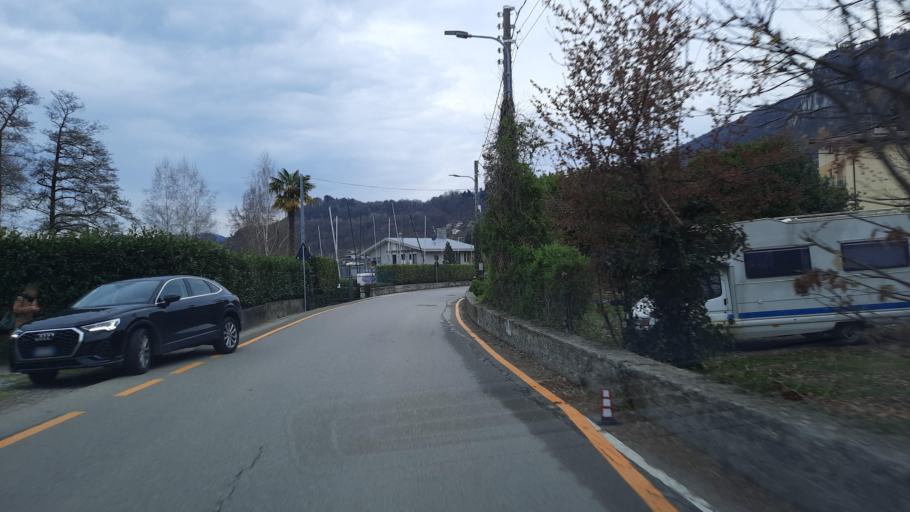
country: IT
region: Piedmont
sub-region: Provincia di Novara
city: Pella
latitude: 45.7979
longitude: 8.3846
